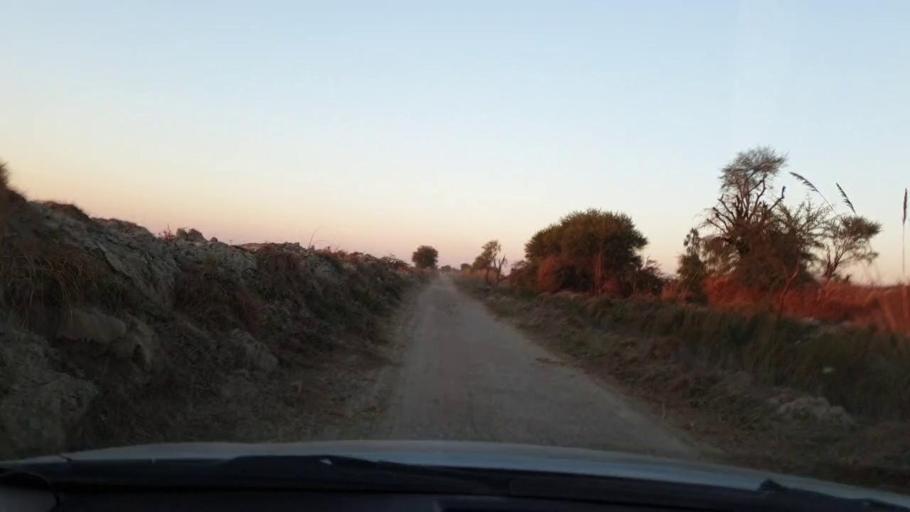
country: PK
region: Sindh
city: Jhol
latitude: 25.9007
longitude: 68.8864
